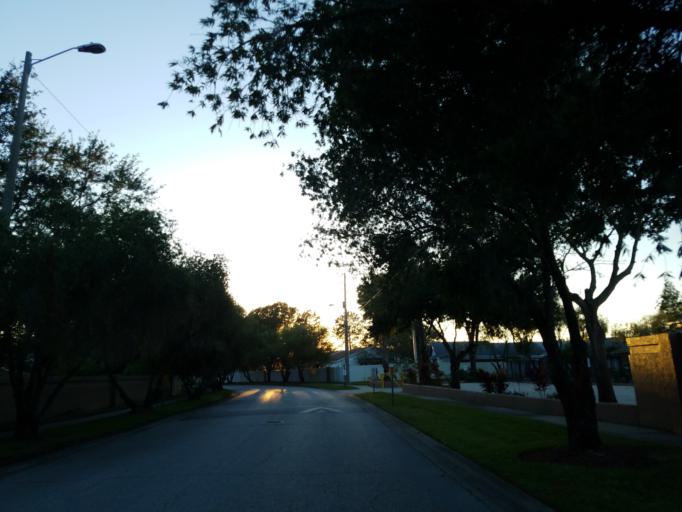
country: US
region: Florida
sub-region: Hillsborough County
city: Brandon
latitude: 27.9254
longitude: -82.3120
